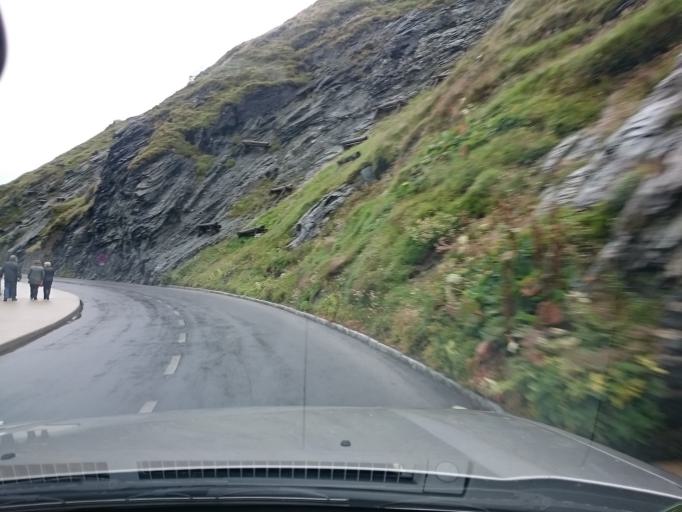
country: AT
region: Carinthia
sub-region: Politischer Bezirk Spittal an der Drau
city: Heiligenblut
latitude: 47.0734
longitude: 12.7550
